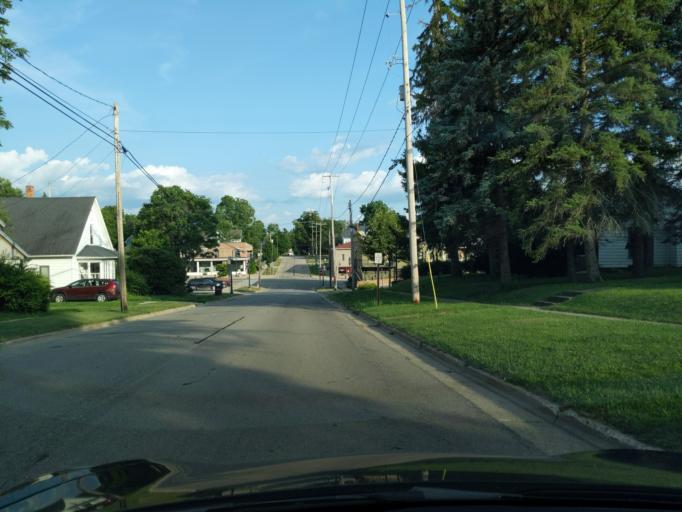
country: US
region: Michigan
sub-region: Eaton County
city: Grand Ledge
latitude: 42.7567
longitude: -84.7427
